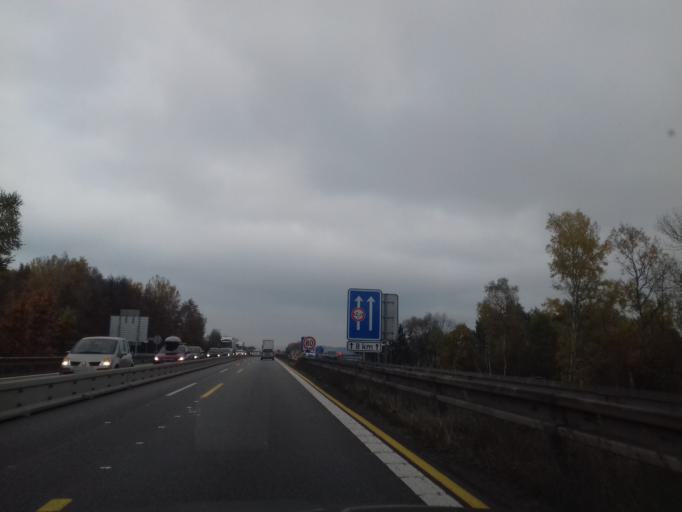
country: CZ
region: Central Bohemia
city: Trhovy Stepanov
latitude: 49.7228
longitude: 15.0493
